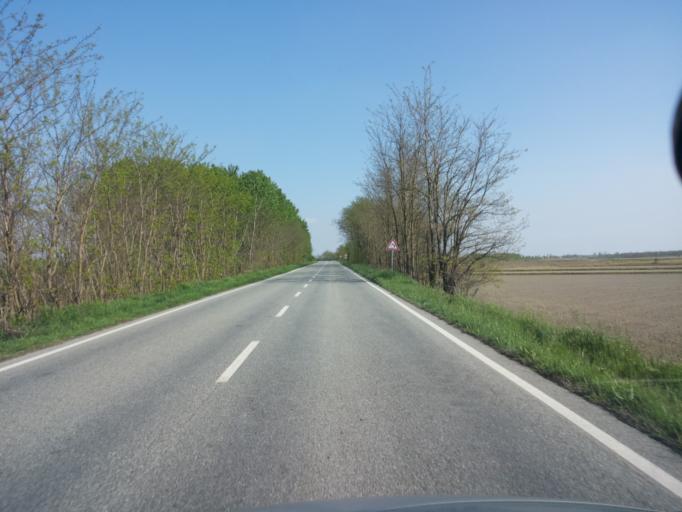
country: IT
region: Piedmont
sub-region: Provincia di Vercelli
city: Motta De Conti
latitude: 45.2063
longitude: 8.5348
